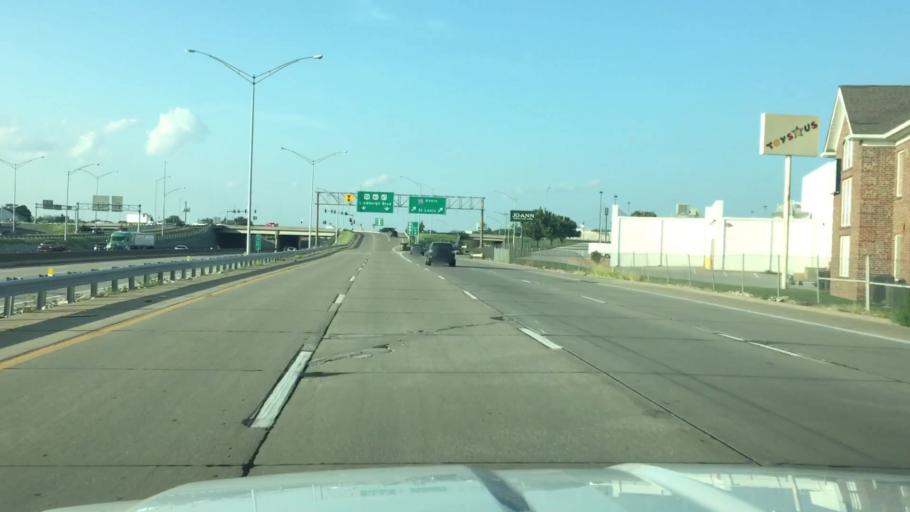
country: US
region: Missouri
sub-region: Saint Louis County
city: Mehlville
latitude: 38.5084
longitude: -90.3364
